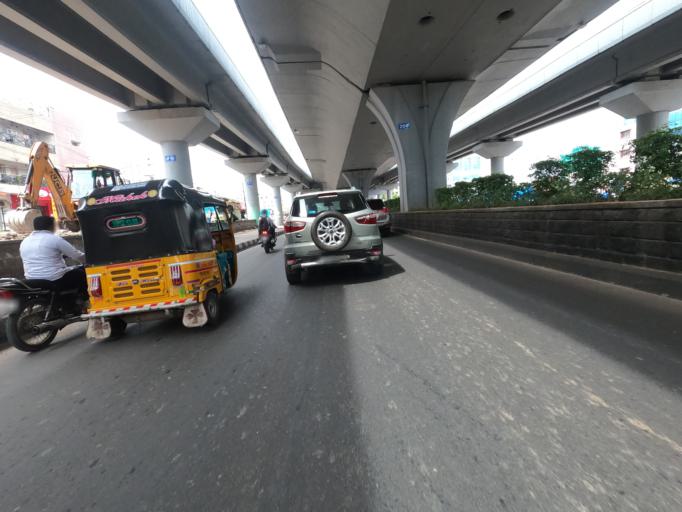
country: IN
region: Telangana
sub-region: Hyderabad
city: Hyderabad
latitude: 17.3486
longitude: 78.4167
